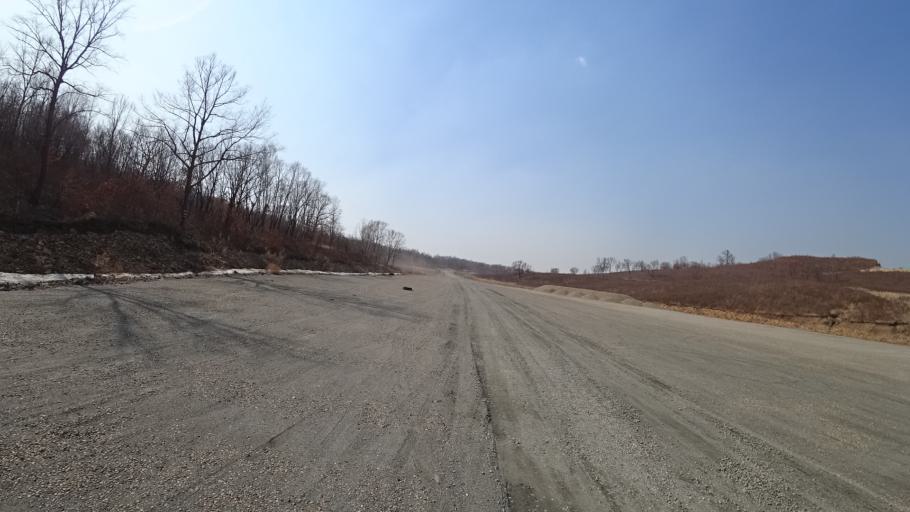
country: RU
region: Amur
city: Novobureyskiy
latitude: 49.8207
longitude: 130.0029
